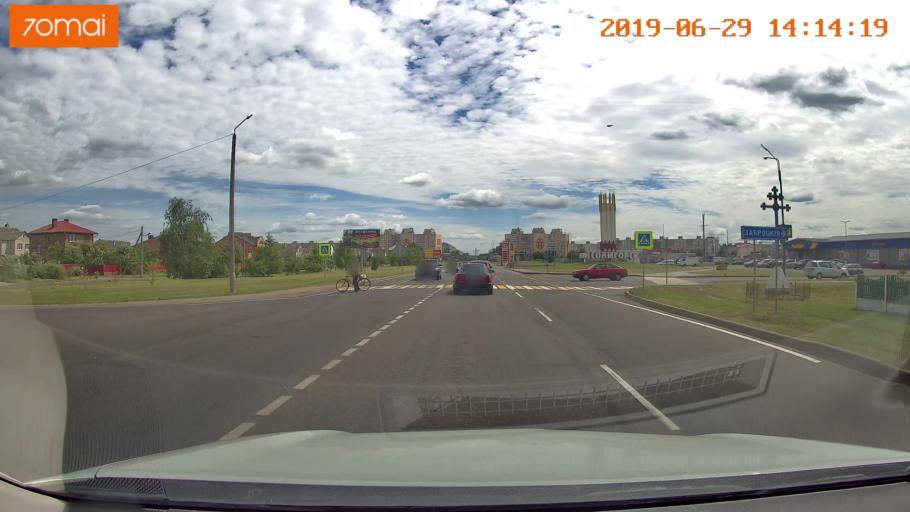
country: BY
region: Minsk
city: Salihorsk
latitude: 52.7963
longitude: 27.5157
